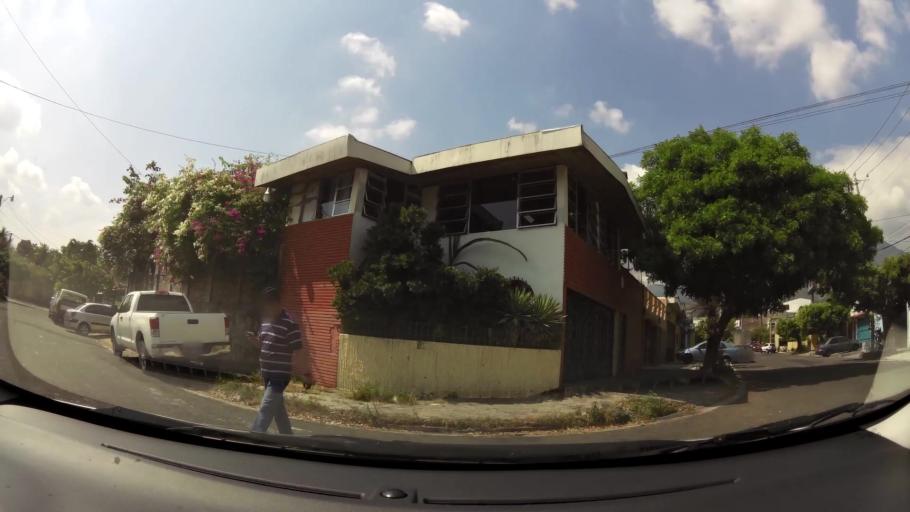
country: SV
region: San Salvador
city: Mejicanos
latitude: 13.7121
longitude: -89.2228
